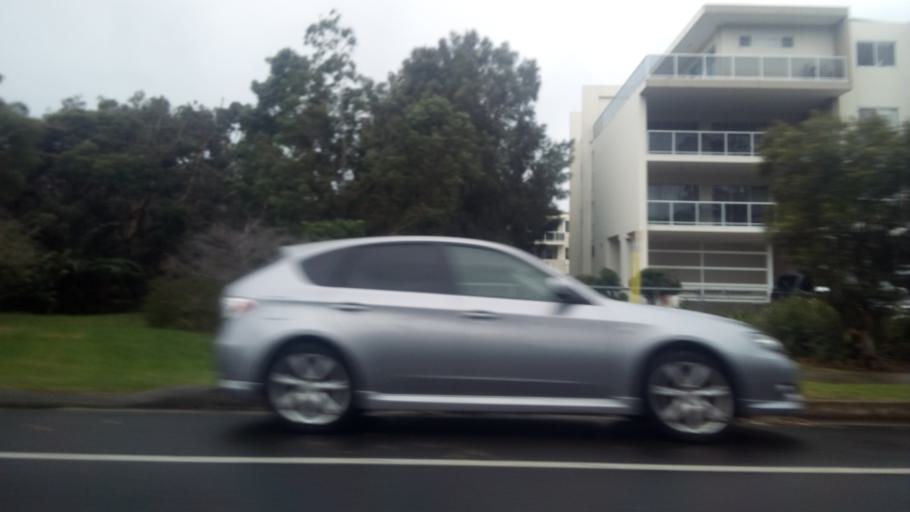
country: AU
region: New South Wales
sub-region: Wollongong
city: Corrimal
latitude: -34.3877
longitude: 150.9026
